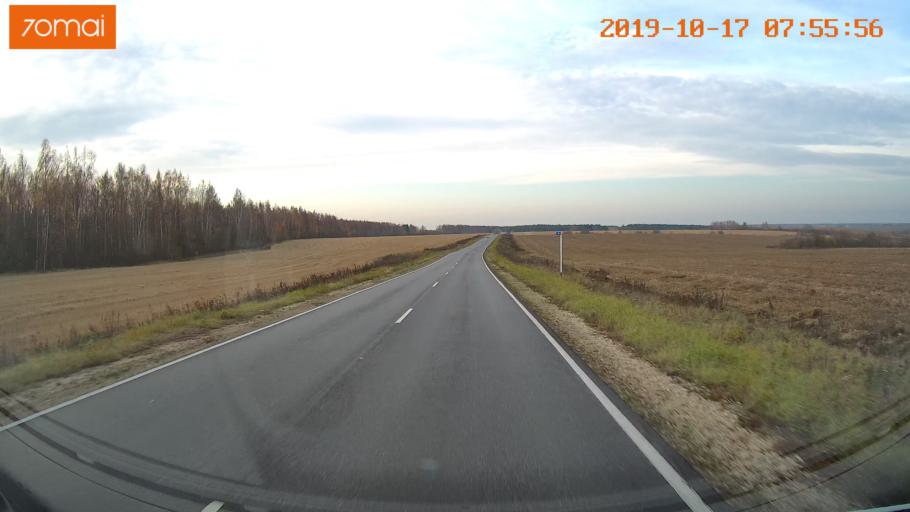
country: RU
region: Vladimir
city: Bavleny
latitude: 56.4295
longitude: 39.5966
